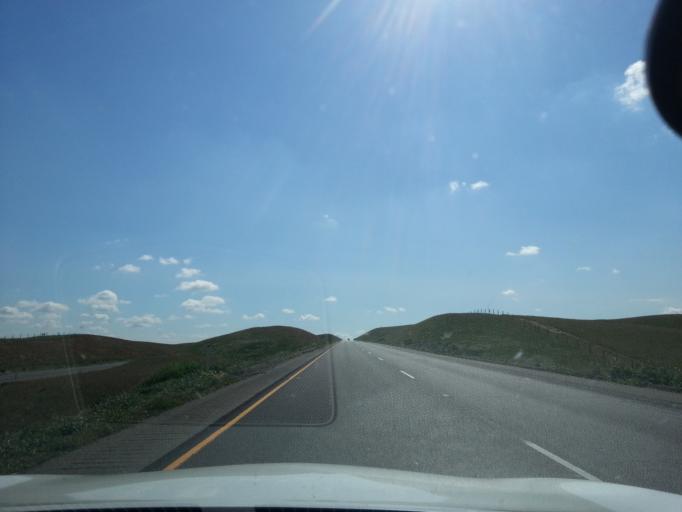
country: US
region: California
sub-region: Fresno County
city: Coalinga
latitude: 36.3278
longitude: -120.2979
